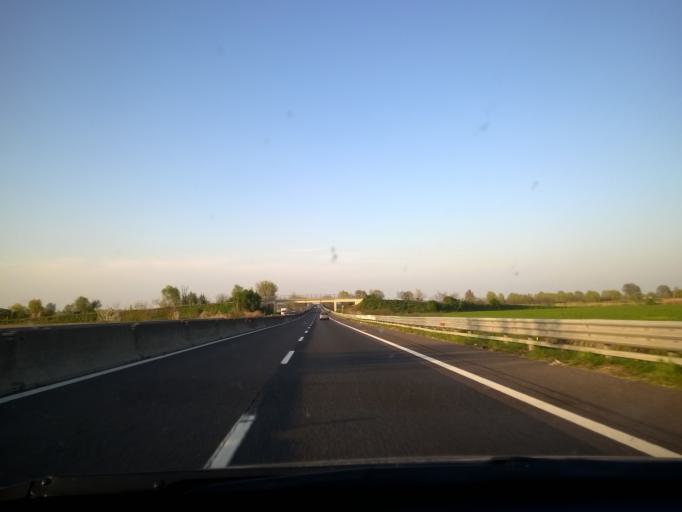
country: IT
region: Emilia-Romagna
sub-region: Provincia di Bologna
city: Malalbergo
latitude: 44.7176
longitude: 11.5038
